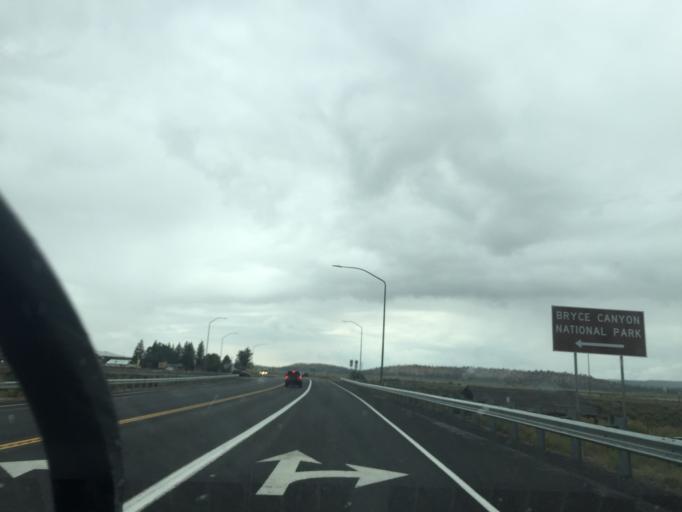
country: US
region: Utah
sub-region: Garfield County
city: Panguitch
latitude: 37.6920
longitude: -112.1505
